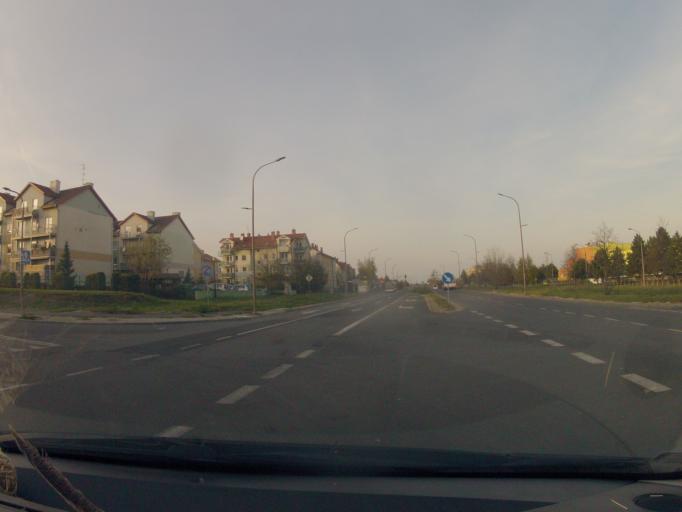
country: PL
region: Opole Voivodeship
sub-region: Powiat opolski
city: Opole
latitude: 50.6755
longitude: 17.9746
